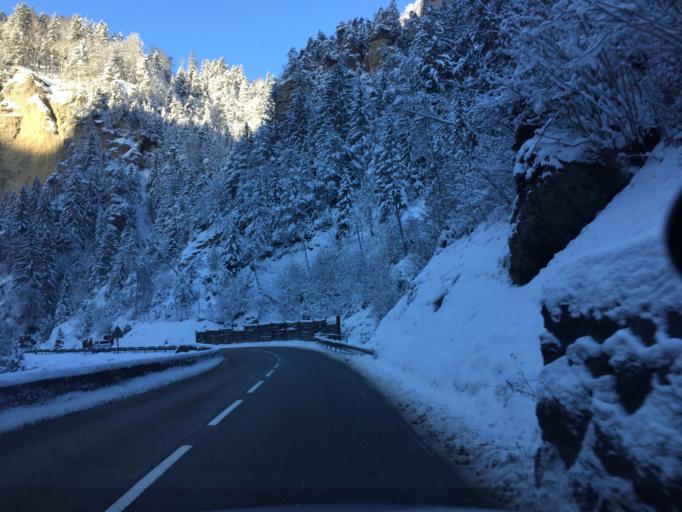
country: FR
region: Rhone-Alpes
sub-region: Departement de la Haute-Savoie
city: Feternes
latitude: 46.3322
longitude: 6.6056
